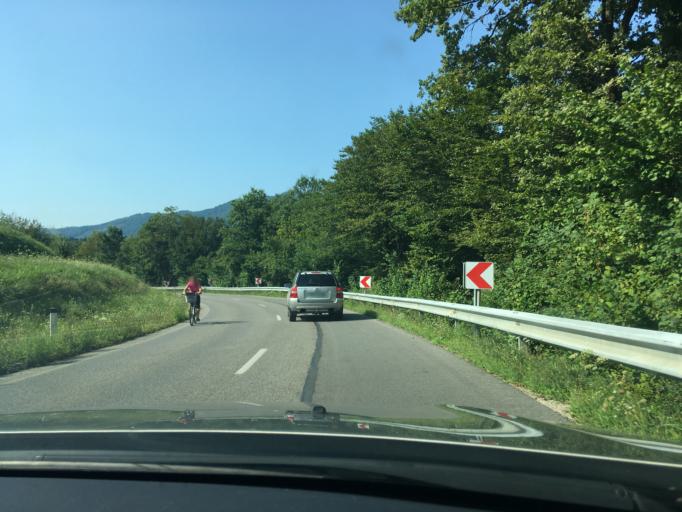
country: SI
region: Dolenjske Toplice
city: Dolenjske Toplice
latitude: 45.7705
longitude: 15.0529
